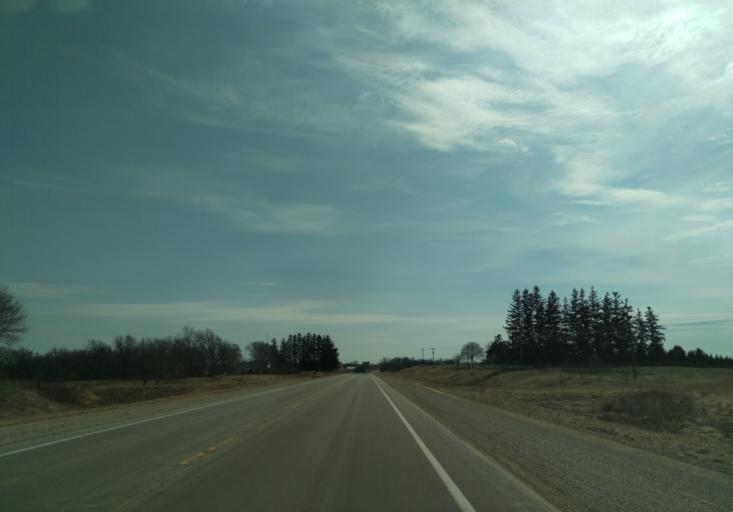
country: US
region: Iowa
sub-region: Winneshiek County
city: Decorah
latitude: 43.4346
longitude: -91.8606
